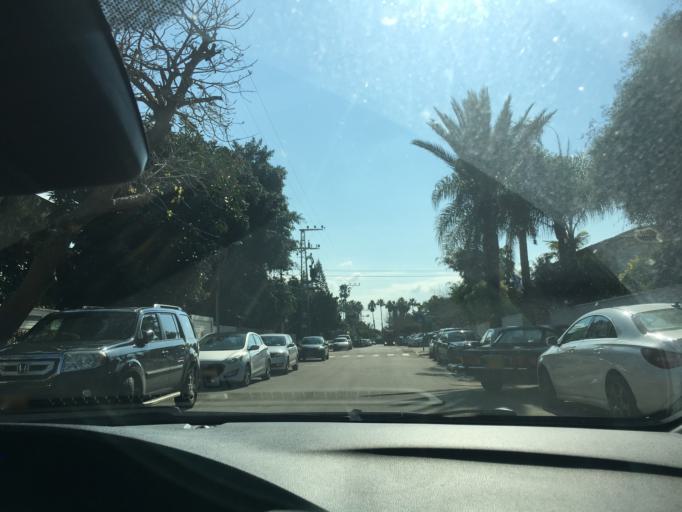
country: IL
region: Tel Aviv
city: Ramat HaSharon
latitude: 32.1498
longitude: 34.8311
